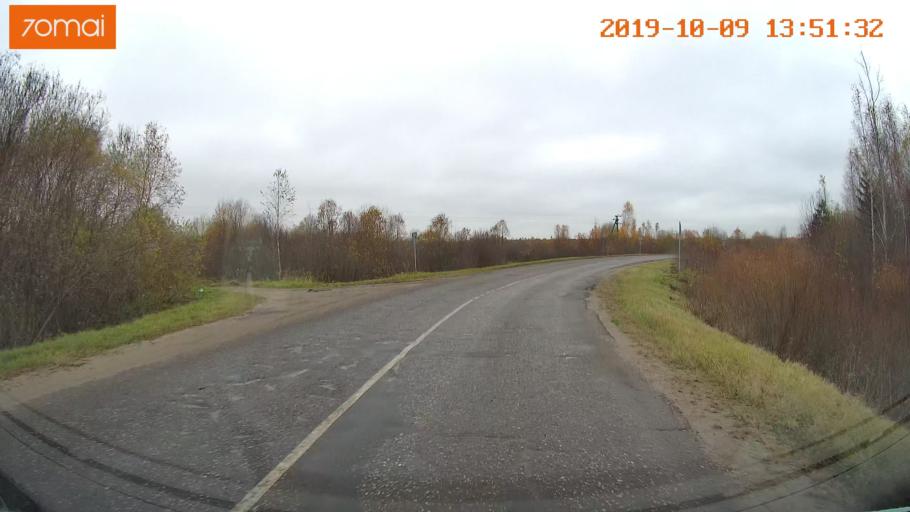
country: RU
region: Kostroma
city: Buy
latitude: 58.4080
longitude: 41.2406
